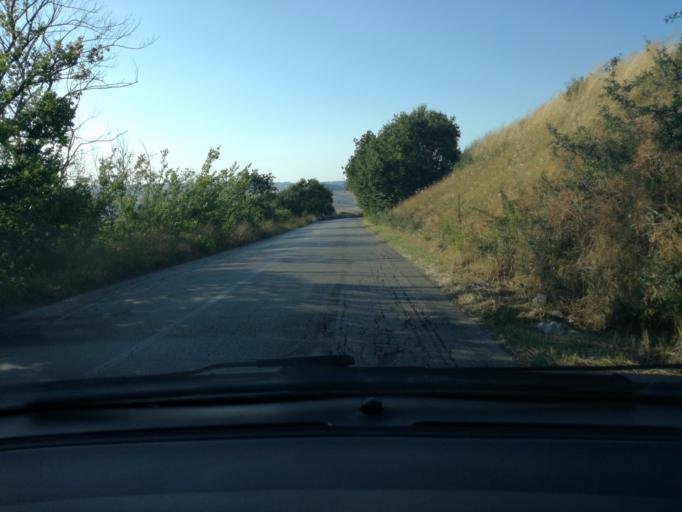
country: IT
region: Molise
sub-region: Provincia di Campobasso
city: Guglionesi
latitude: 41.9325
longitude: 14.9313
